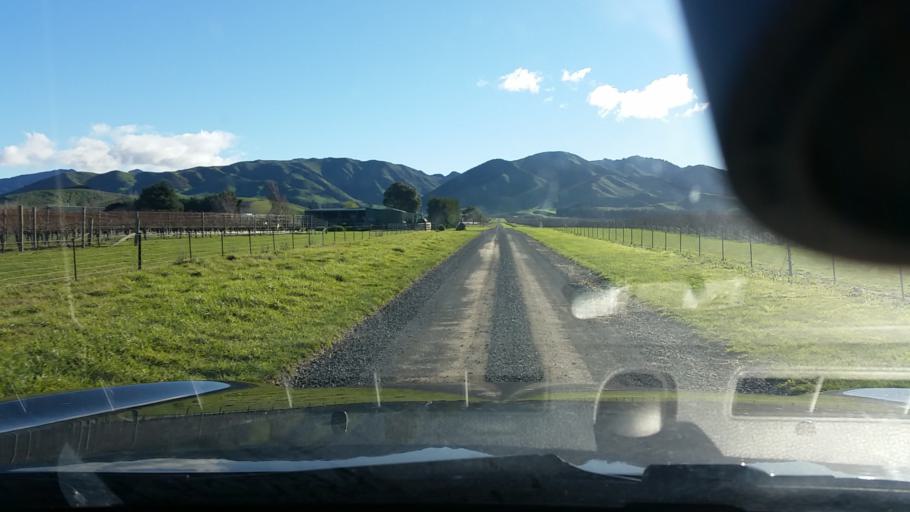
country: NZ
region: Marlborough
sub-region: Marlborough District
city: Blenheim
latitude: -41.6456
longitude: 174.0501
